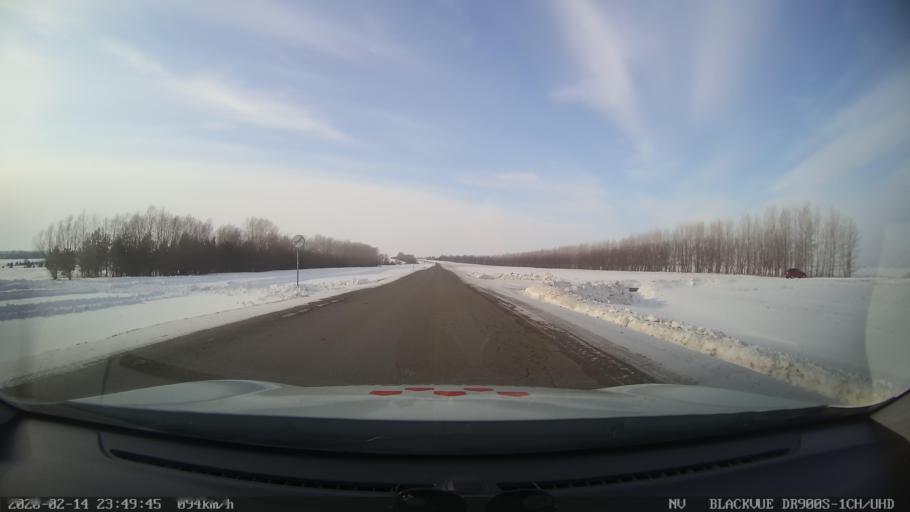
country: RU
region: Tatarstan
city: Kuybyshevskiy Zaton
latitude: 55.2558
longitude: 49.1739
